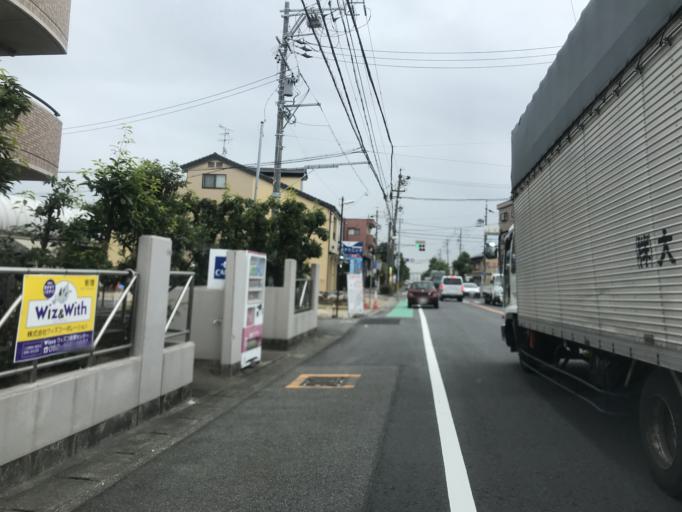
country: JP
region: Aichi
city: Nagoya-shi
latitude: 35.2062
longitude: 136.8397
